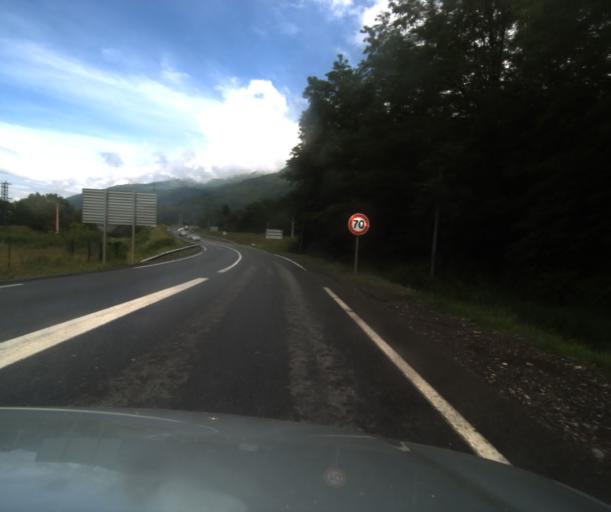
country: FR
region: Midi-Pyrenees
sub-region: Departement des Hautes-Pyrenees
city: Pierrefitte-Nestalas
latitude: 42.9516
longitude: -0.0667
